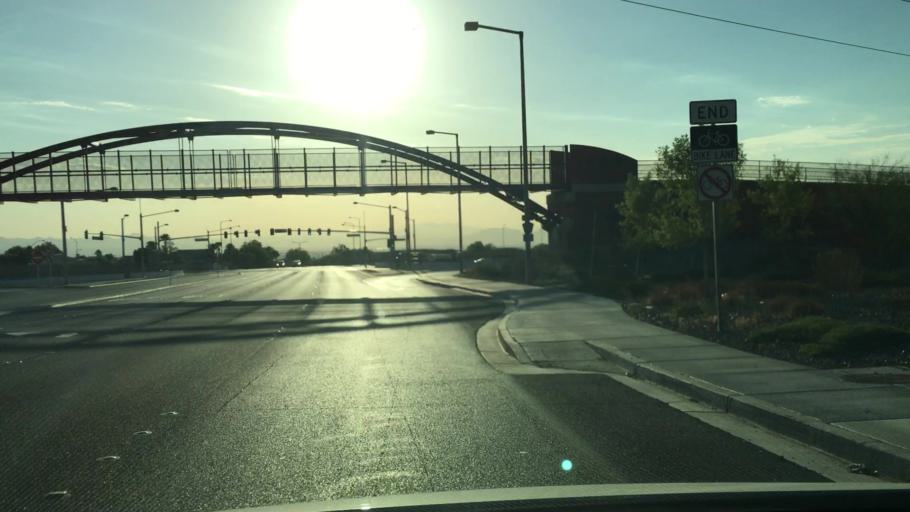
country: US
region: Nevada
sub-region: Clark County
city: Summerlin South
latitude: 36.1809
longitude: -115.3431
